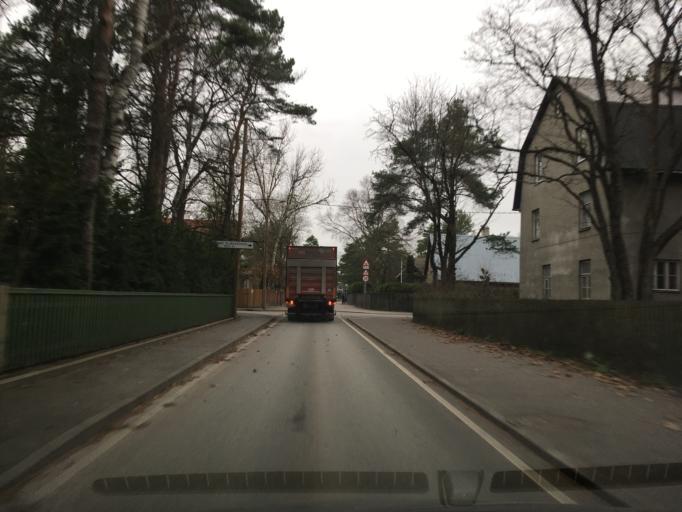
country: EE
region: Harju
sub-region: Saue vald
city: Laagri
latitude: 59.3822
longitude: 24.6731
